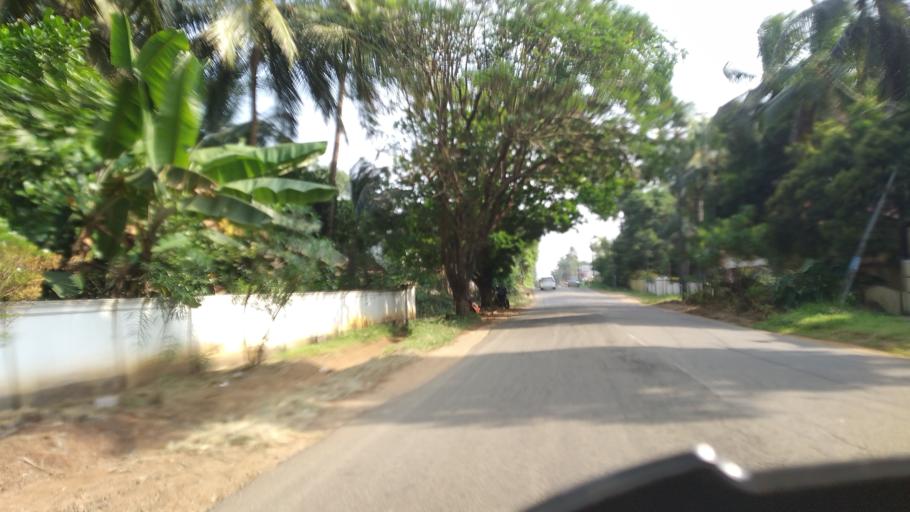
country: IN
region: Kerala
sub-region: Thrissur District
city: Chelakara
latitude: 10.5940
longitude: 76.5032
